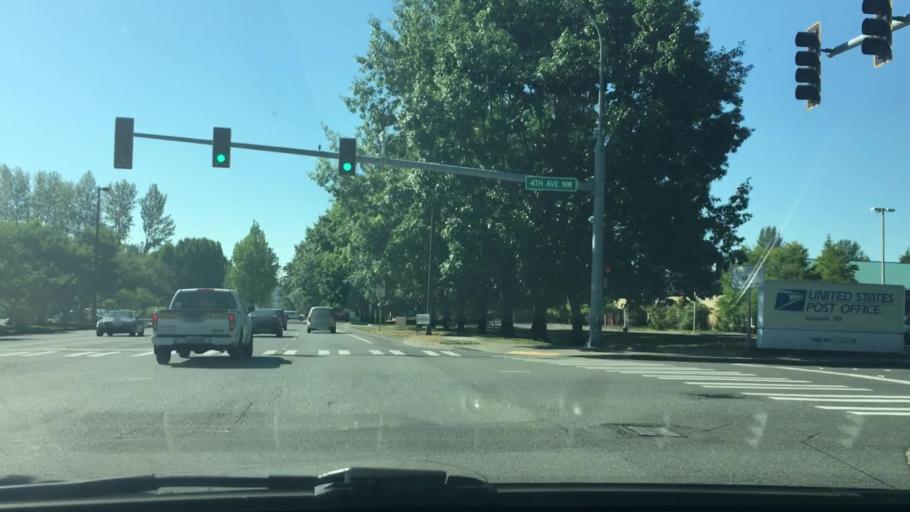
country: US
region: Washington
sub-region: King County
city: Issaquah
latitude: 47.5412
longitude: -122.0419
